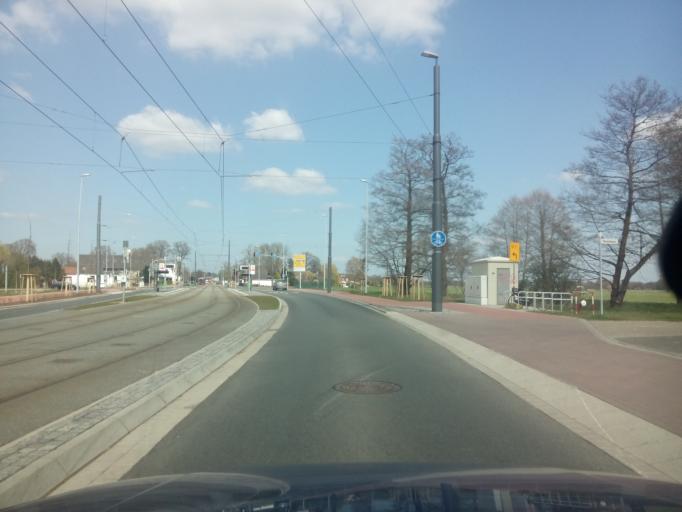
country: DE
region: Lower Saxony
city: Lilienthal
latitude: 53.1534
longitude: 8.9377
